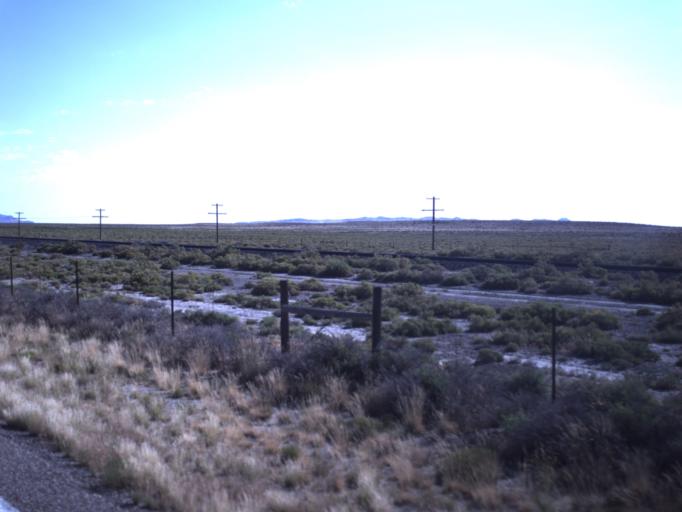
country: US
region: Utah
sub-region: Beaver County
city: Milford
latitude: 38.6271
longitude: -112.9845
